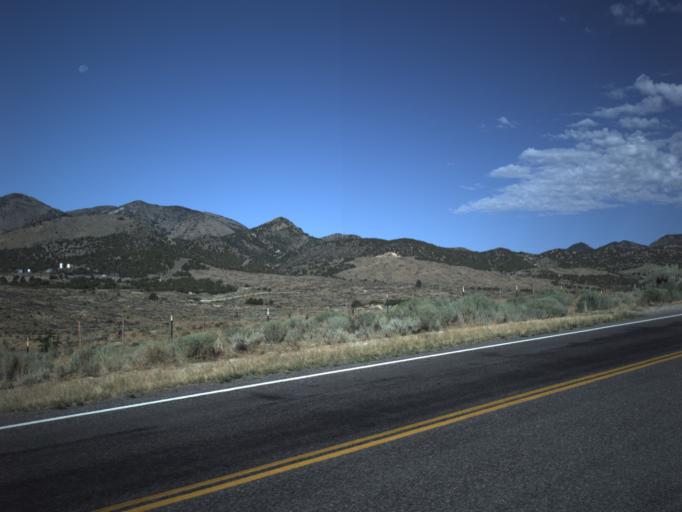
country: US
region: Utah
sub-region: Utah County
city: Genola
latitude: 39.9536
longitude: -112.0316
